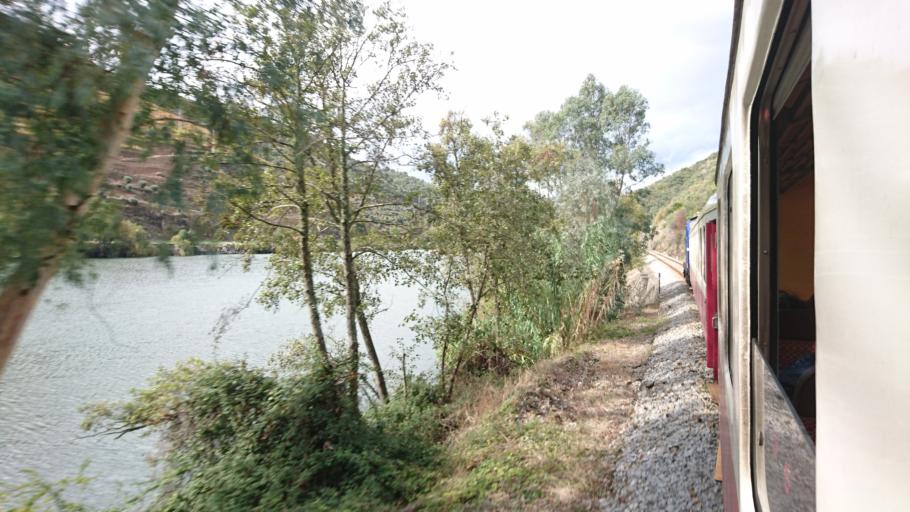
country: PT
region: Viseu
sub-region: Armamar
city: Armamar
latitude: 41.1448
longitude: -7.7105
